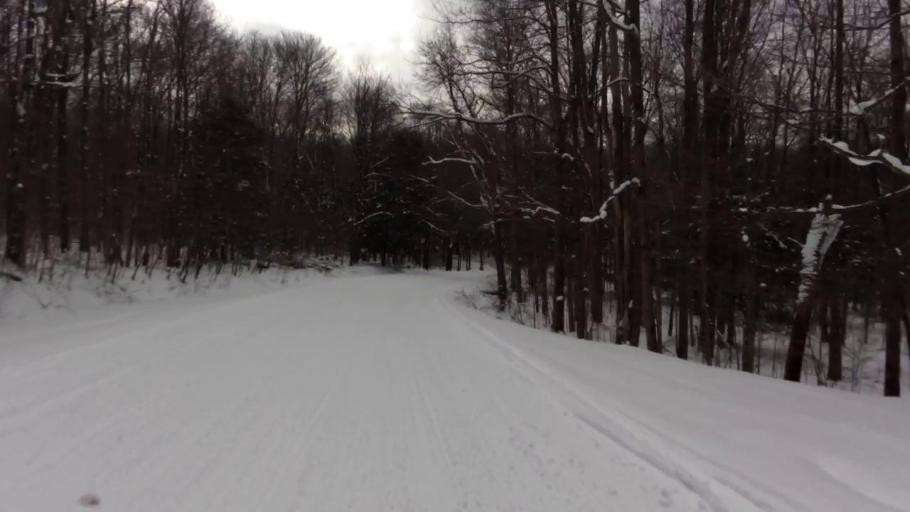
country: US
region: New York
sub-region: Cattaraugus County
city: Salamanca
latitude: 42.0372
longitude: -78.7869
